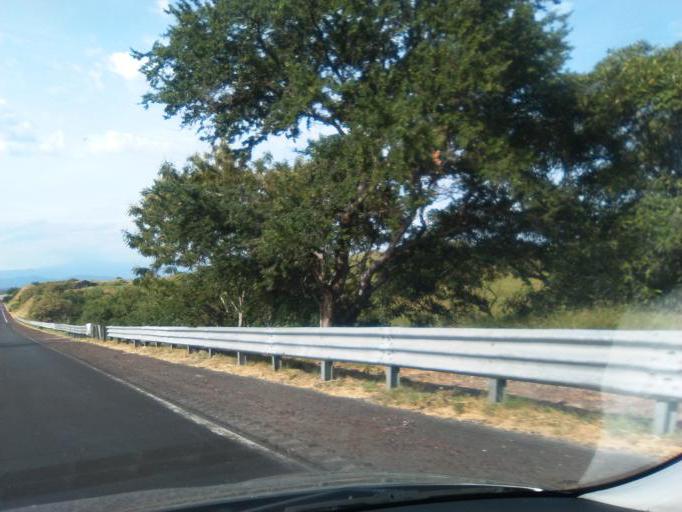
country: MX
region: Morelos
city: Puente de Ixtla
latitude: 18.6095
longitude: -99.2878
